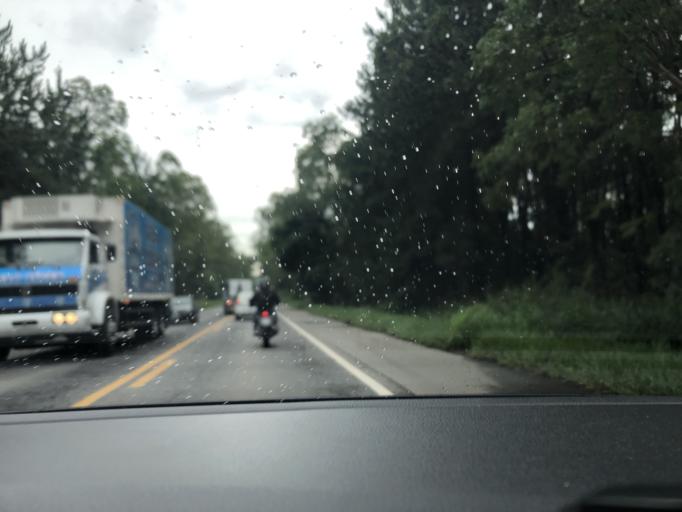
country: BR
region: Sao Paulo
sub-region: Jarinu
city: Jarinu
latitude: -23.1244
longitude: -46.7345
